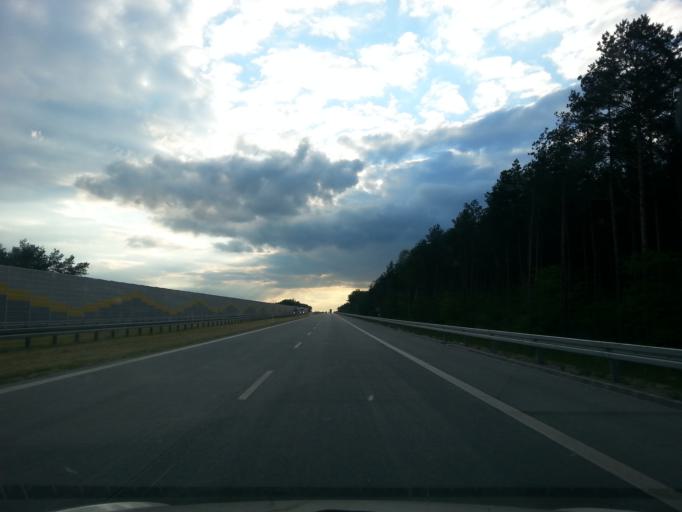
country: PL
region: Lodz Voivodeship
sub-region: Powiat zdunskowolski
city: Zdunska Wola
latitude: 51.5695
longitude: 18.9696
